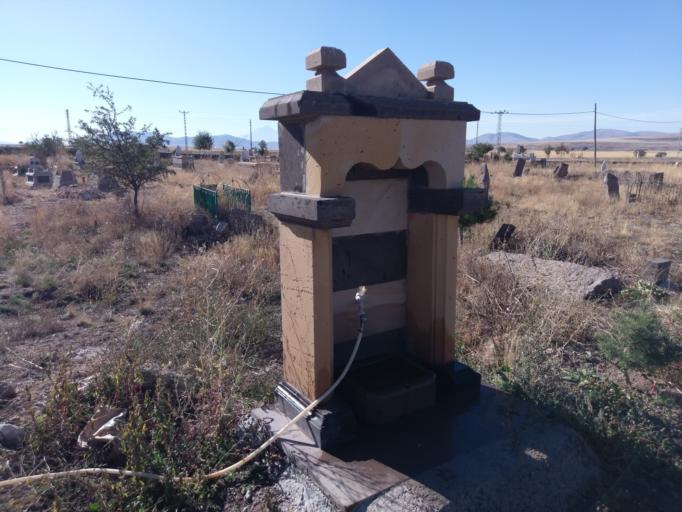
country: TR
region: Kayseri
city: Toklar
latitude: 38.4268
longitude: 36.0927
